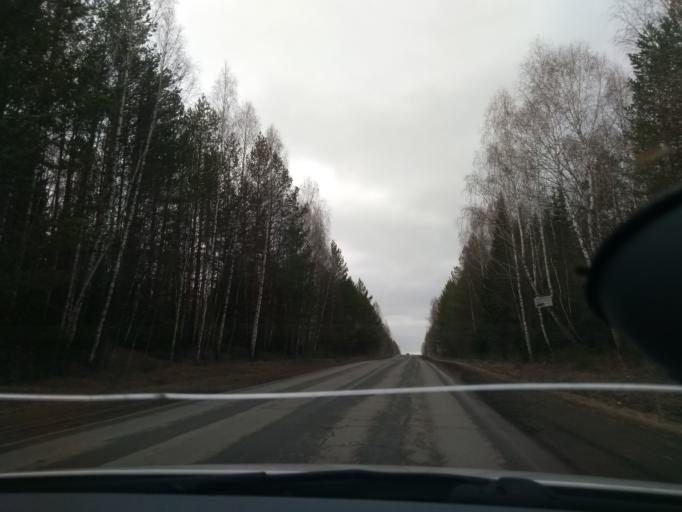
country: RU
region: Perm
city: Kungur
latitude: 57.3561
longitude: 56.8086
